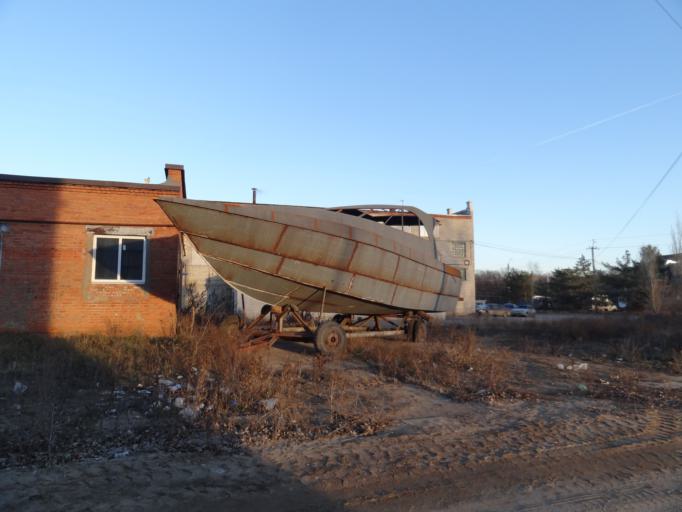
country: RU
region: Saratov
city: Engel's
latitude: 51.4792
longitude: 46.0563
